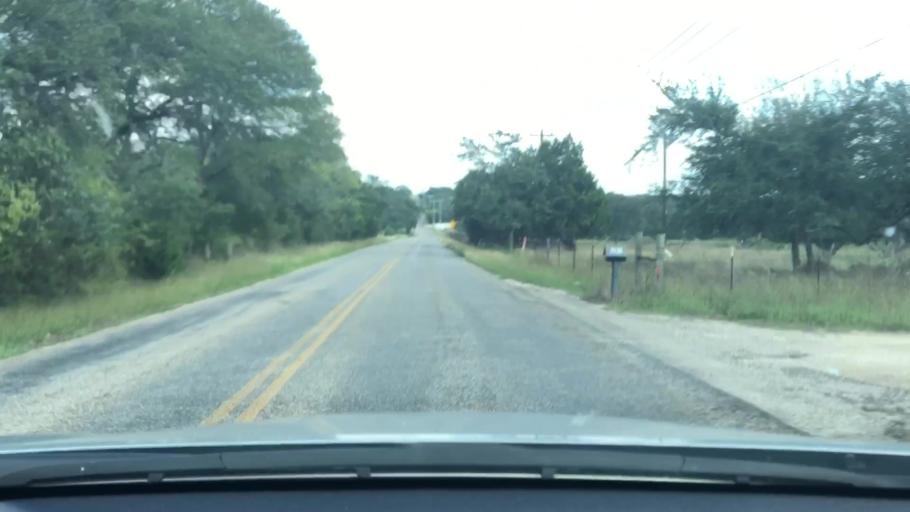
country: US
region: Texas
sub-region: Bexar County
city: Fair Oaks Ranch
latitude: 29.7853
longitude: -98.6358
